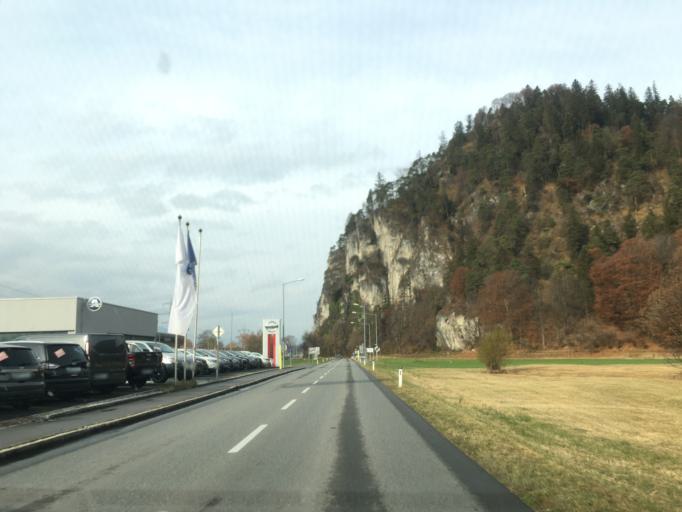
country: AT
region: Vorarlberg
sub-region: Politischer Bezirk Bludenz
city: Nuziders
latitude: 47.1752
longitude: 9.7857
